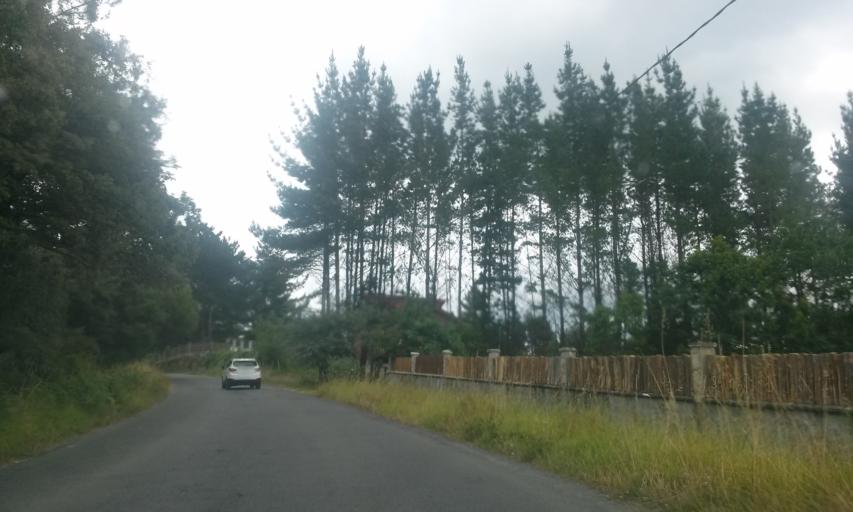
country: ES
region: Galicia
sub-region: Provincia de Lugo
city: Outeiro de Rei
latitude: 43.0671
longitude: -7.6257
